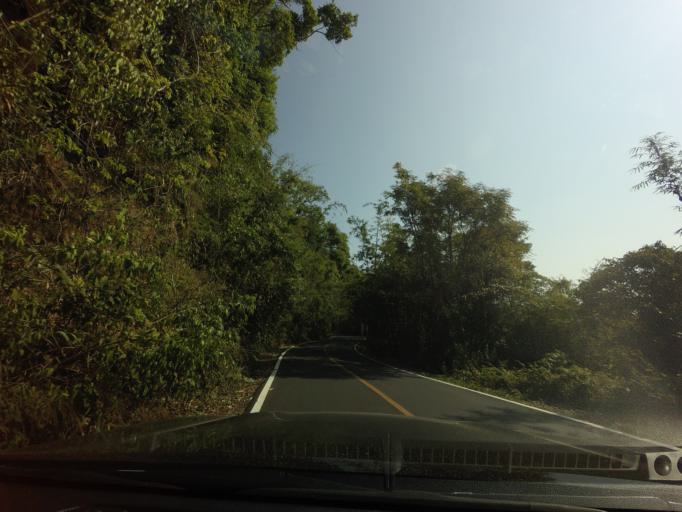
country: TH
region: Kanchanaburi
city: Thong Pha Phum
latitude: 14.6837
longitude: 98.4179
